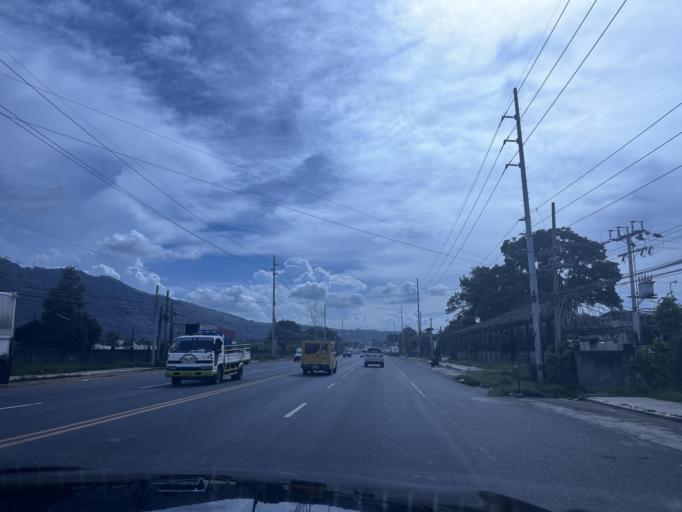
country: PH
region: Northern Mindanao
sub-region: Chartered City of Cagayan de Oro
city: Agusan
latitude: 8.4768
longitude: 124.7189
